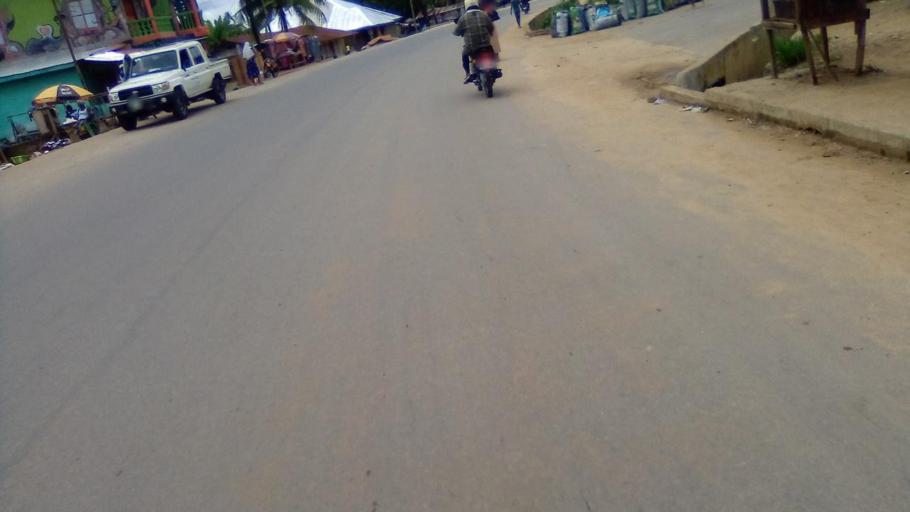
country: SL
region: Southern Province
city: Bo
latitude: 7.9520
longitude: -11.7547
